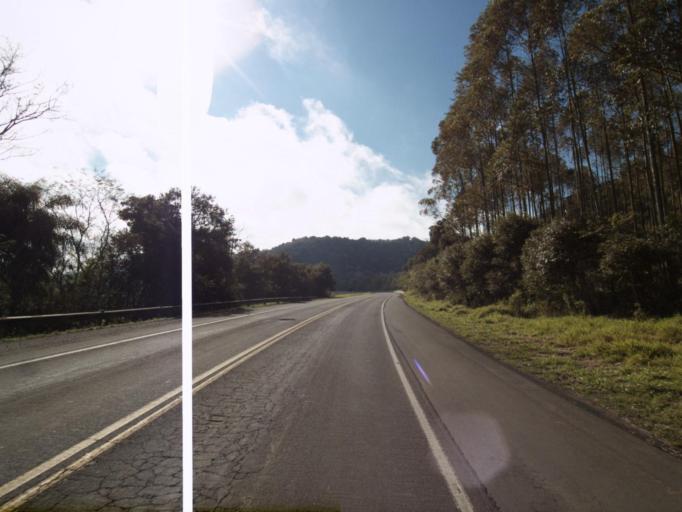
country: BR
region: Rio Grande do Sul
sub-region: Frederico Westphalen
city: Frederico Westphalen
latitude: -27.1588
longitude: -53.2196
